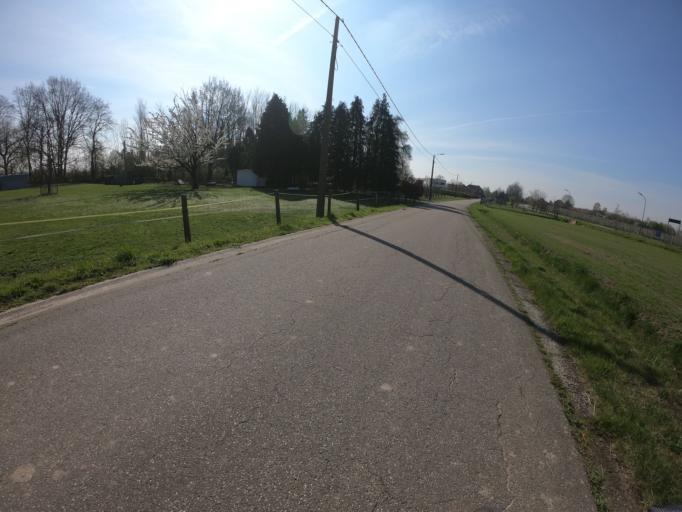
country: BE
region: Flanders
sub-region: Provincie Limburg
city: Herk-de-Stad
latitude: 50.9145
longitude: 5.1776
